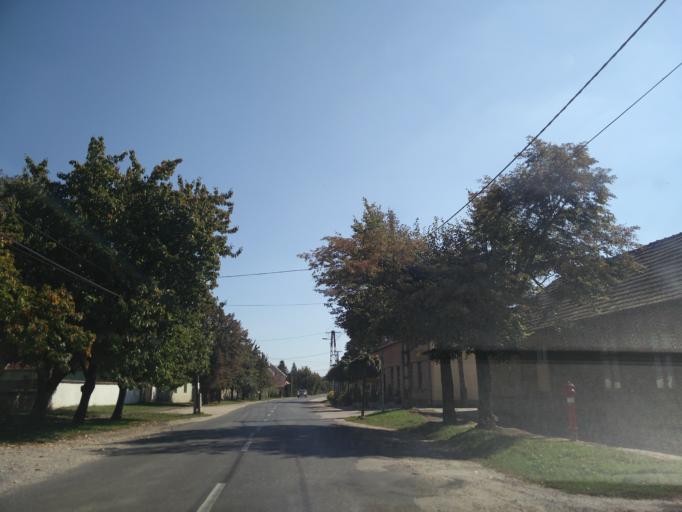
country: HU
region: Fejer
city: Lovasbereny
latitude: 47.3131
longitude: 18.5482
